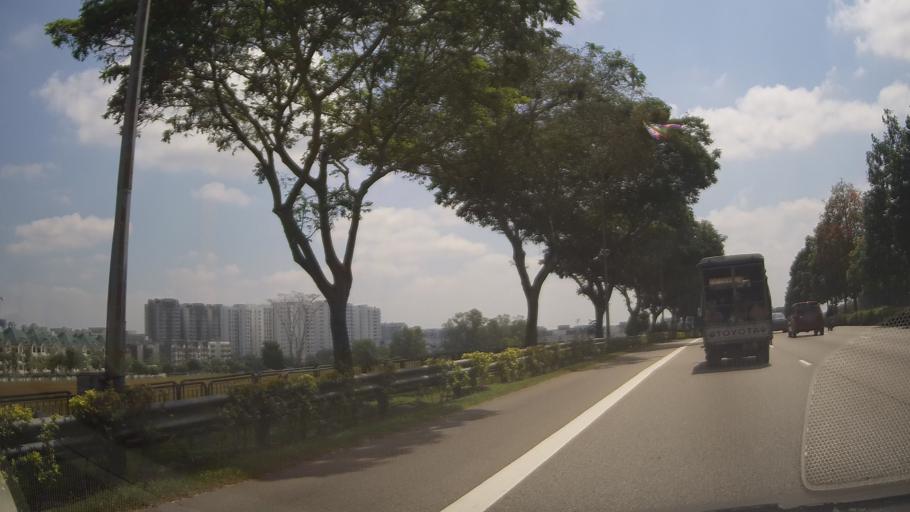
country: MY
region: Johor
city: Johor Bahru
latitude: 1.4265
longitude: 103.7808
